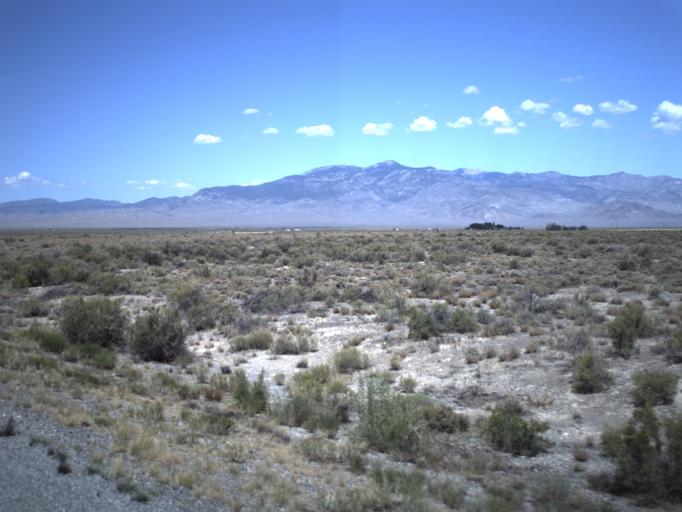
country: US
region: Nevada
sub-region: White Pine County
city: McGill
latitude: 39.0506
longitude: -113.9628
